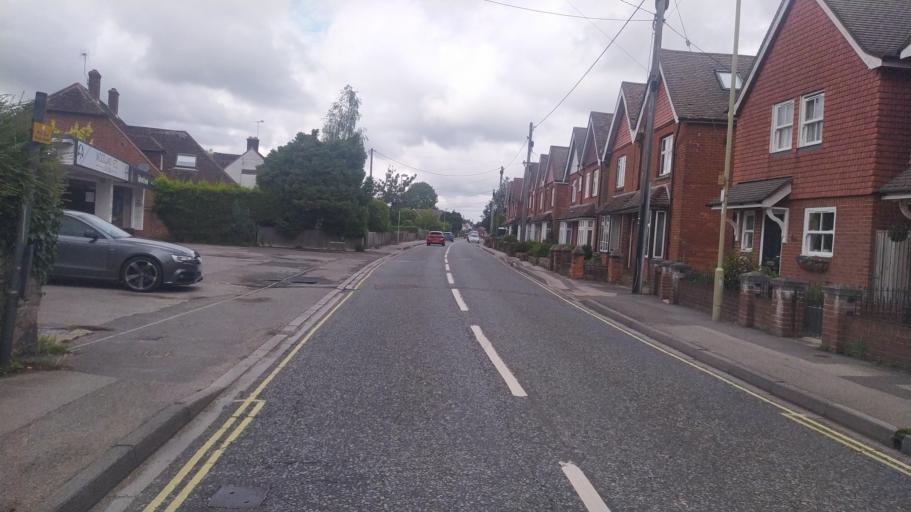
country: GB
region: England
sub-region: Hampshire
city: Liphook
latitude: 51.0781
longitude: -0.8037
